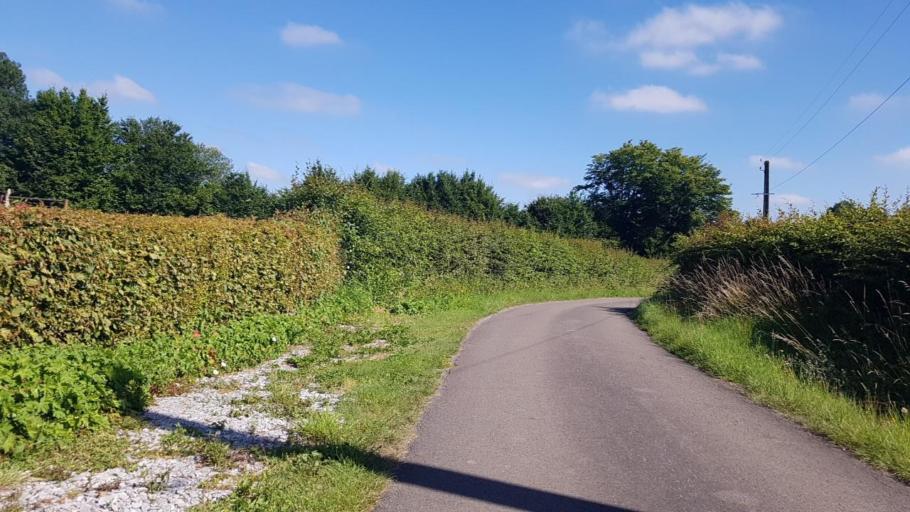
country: FR
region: Nord-Pas-de-Calais
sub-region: Departement du Nord
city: Anor
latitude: 49.9892
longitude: 4.1324
